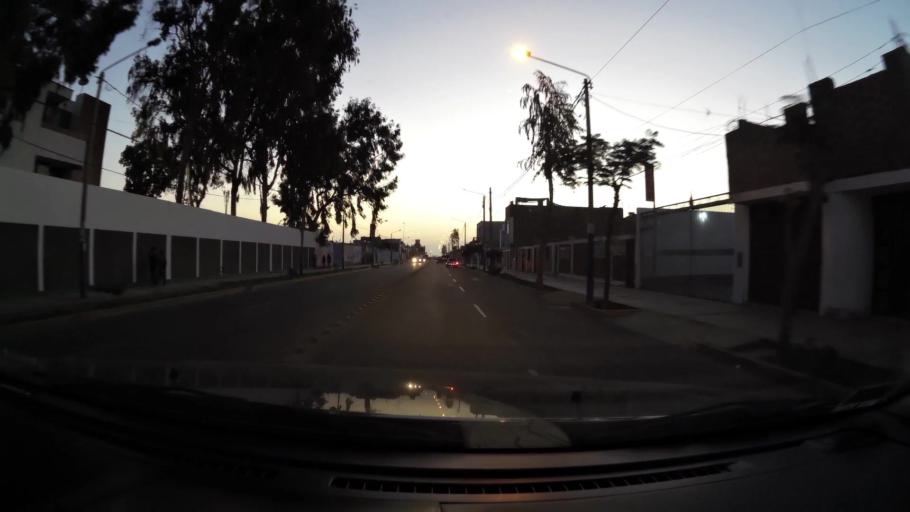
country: PE
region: Ica
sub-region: Provincia de Pisco
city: Pisco
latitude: -13.7096
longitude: -76.2141
